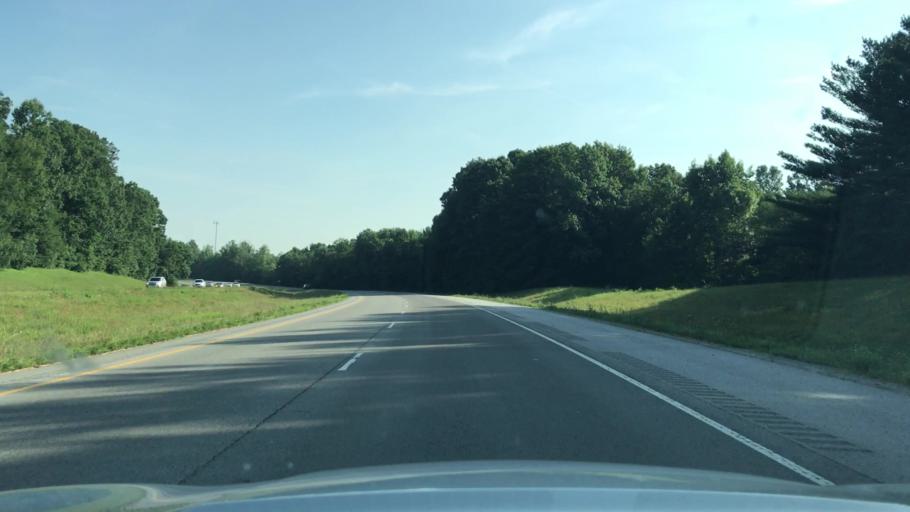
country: US
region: Tennessee
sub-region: Putnam County
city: Algood
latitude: 36.1705
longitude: -85.4617
